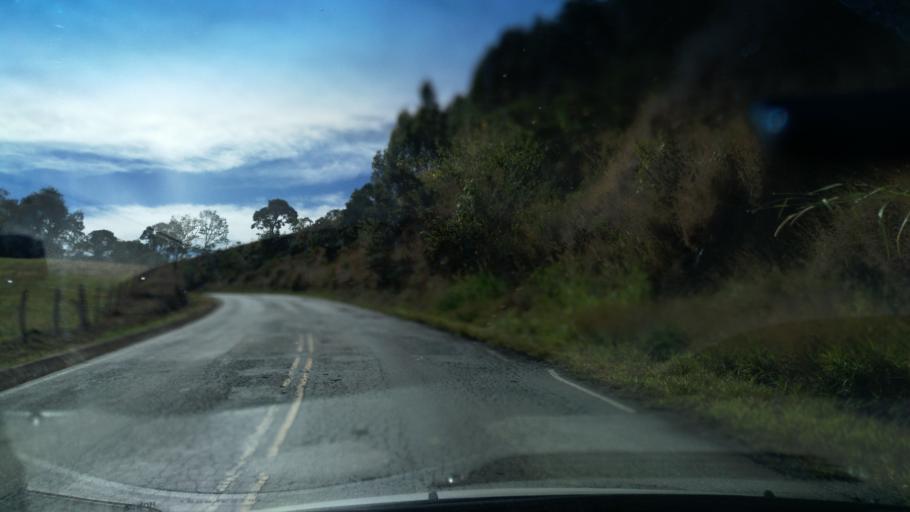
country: BR
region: Minas Gerais
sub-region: Andradas
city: Andradas
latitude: -22.0522
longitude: -46.3609
